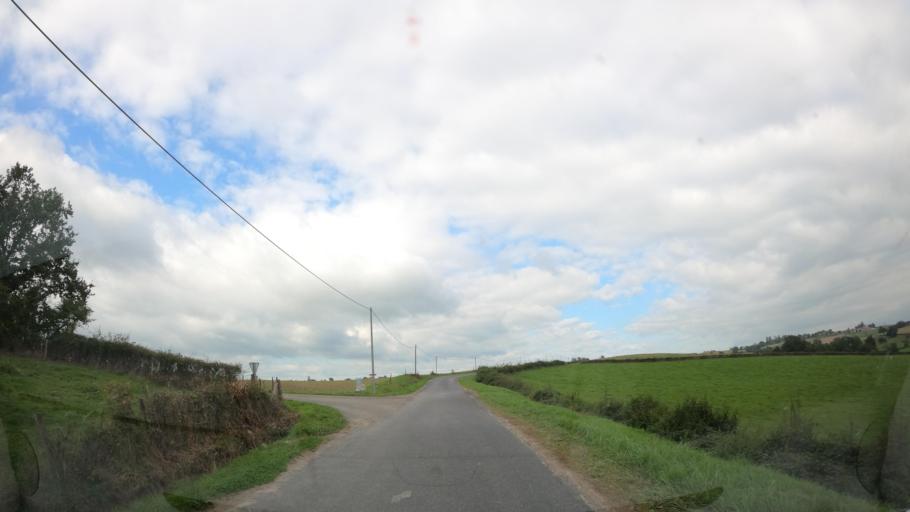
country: FR
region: Auvergne
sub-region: Departement de l'Allier
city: Lapalisse
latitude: 46.3317
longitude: 3.6305
